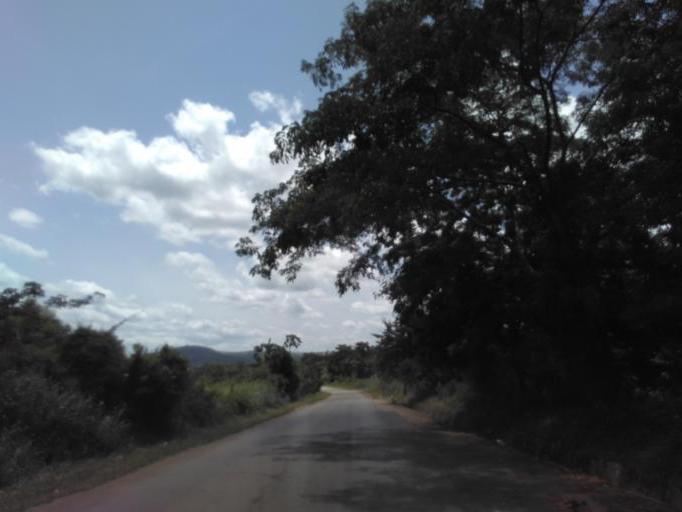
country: GH
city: Akropong
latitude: 6.0876
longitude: -0.1004
